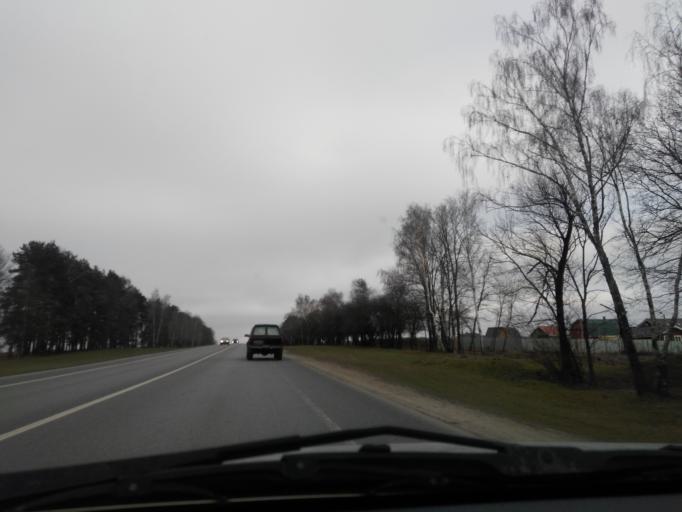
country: RU
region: Moskovskaya
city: Troitsk
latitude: 55.3479
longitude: 37.1780
